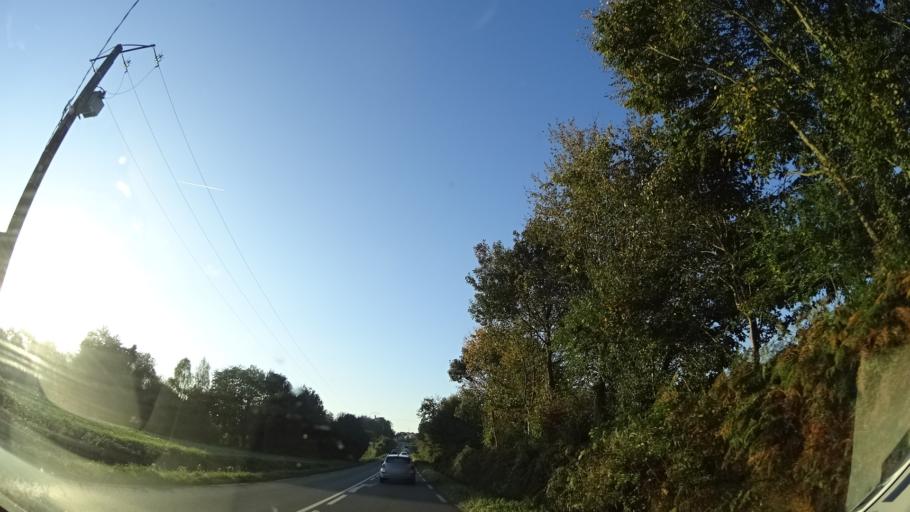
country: FR
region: Brittany
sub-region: Departement d'Ille-et-Vilaine
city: La Meziere
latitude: 48.2054
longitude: -1.7466
